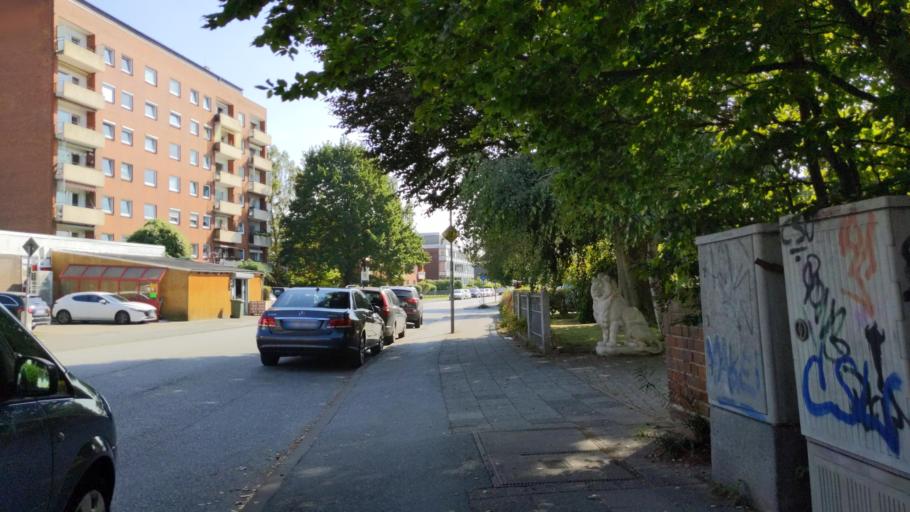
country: DE
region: Schleswig-Holstein
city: Luebeck
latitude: 53.8855
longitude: 10.6789
